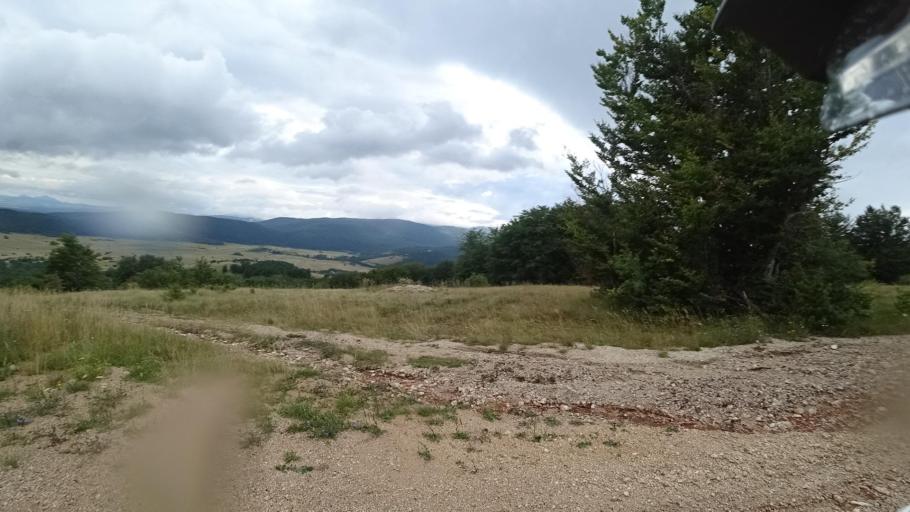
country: HR
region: Licko-Senjska
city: Jezerce
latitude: 44.7296
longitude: 15.6362
